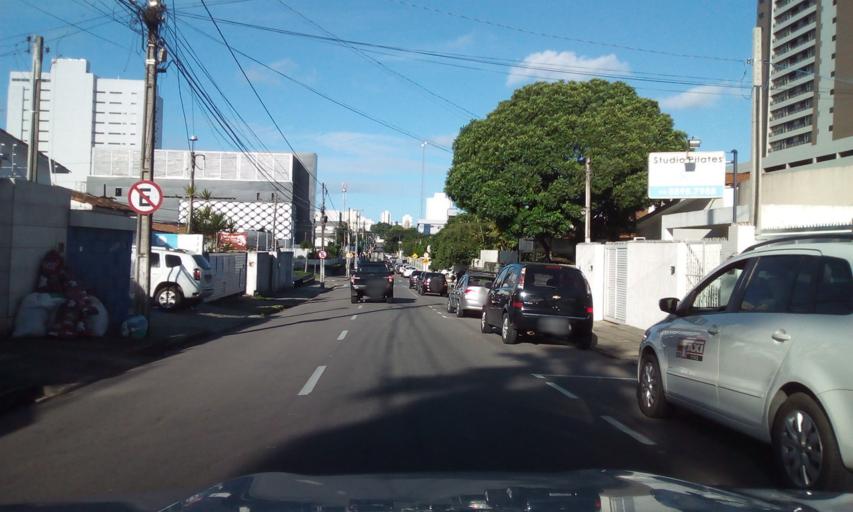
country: BR
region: Paraiba
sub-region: Joao Pessoa
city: Joao Pessoa
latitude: -7.1176
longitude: -34.8578
